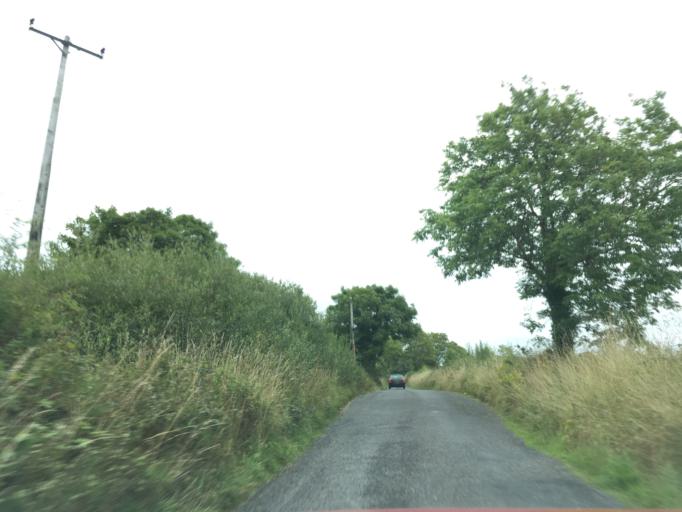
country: IE
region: Munster
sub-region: An Clar
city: Ennis
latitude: 52.7194
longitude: -9.0851
